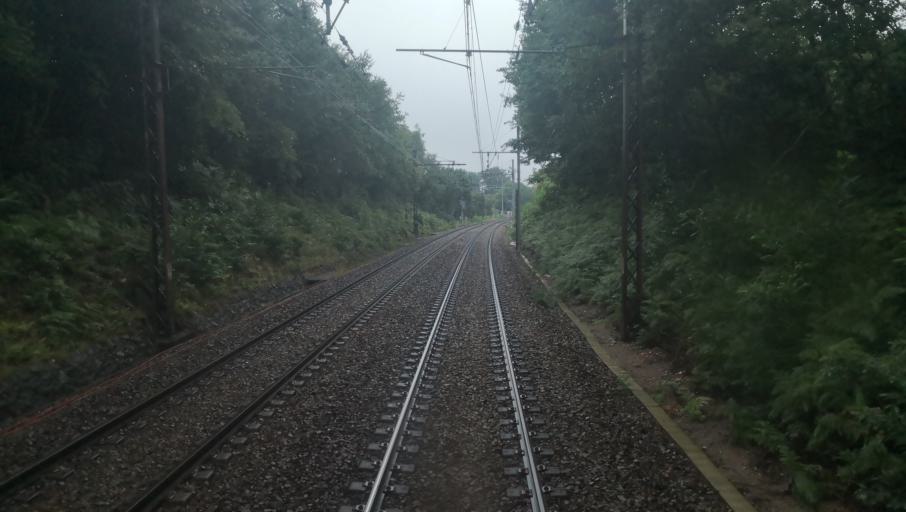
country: FR
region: Limousin
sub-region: Departement de la Creuse
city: La Souterraine
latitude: 46.2566
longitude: 1.4764
